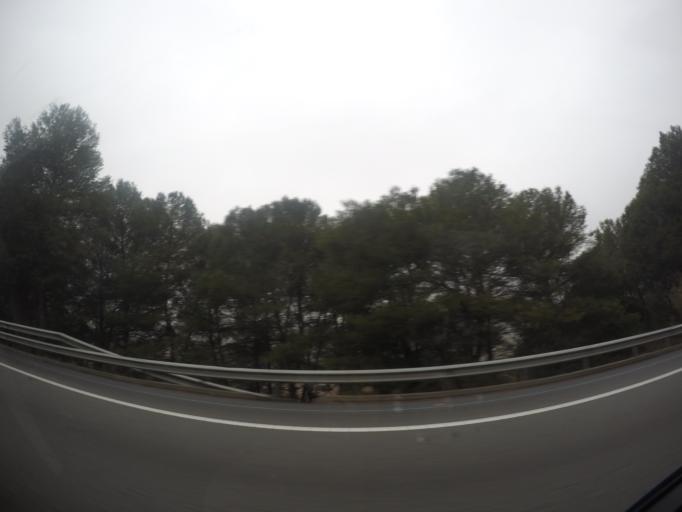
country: ES
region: Catalonia
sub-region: Provincia de Barcelona
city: Gelida
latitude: 41.4377
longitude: 1.8412
